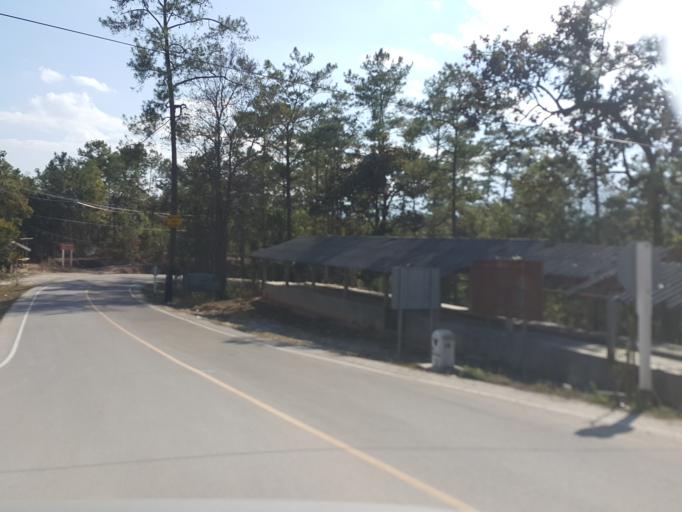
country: TH
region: Chiang Mai
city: Mae Wang
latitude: 18.6974
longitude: 98.5687
